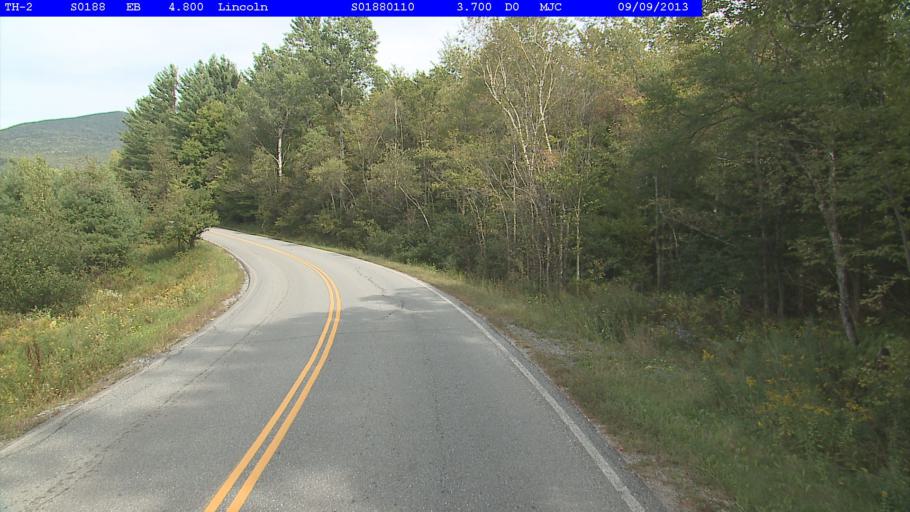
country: US
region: Vermont
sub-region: Addison County
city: Bristol
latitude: 44.0972
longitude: -72.9766
